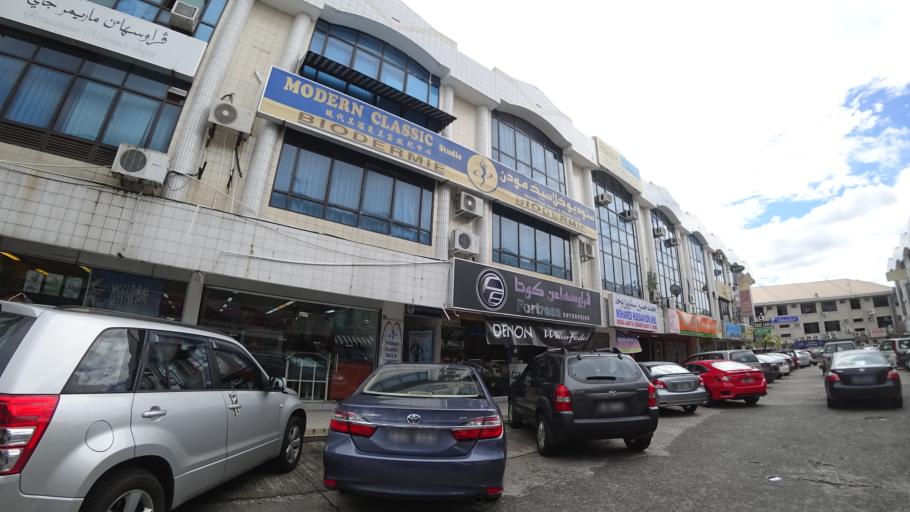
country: BN
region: Brunei and Muara
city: Bandar Seri Begawan
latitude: 4.9004
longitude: 114.9281
